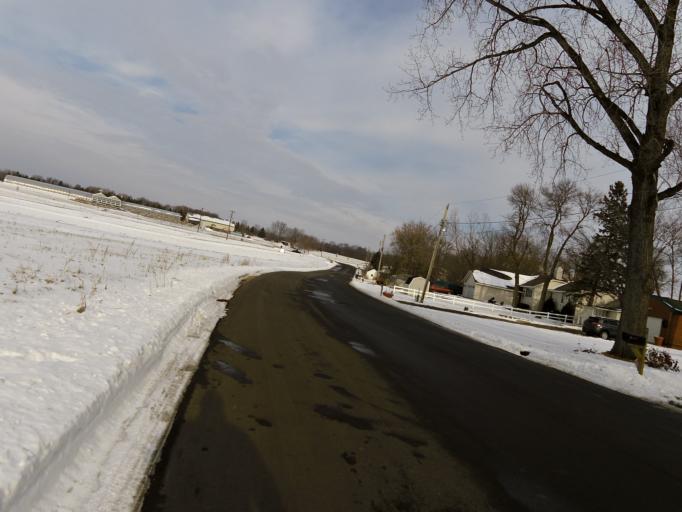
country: US
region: Minnesota
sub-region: Scott County
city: Prior Lake
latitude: 44.7019
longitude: -93.4884
